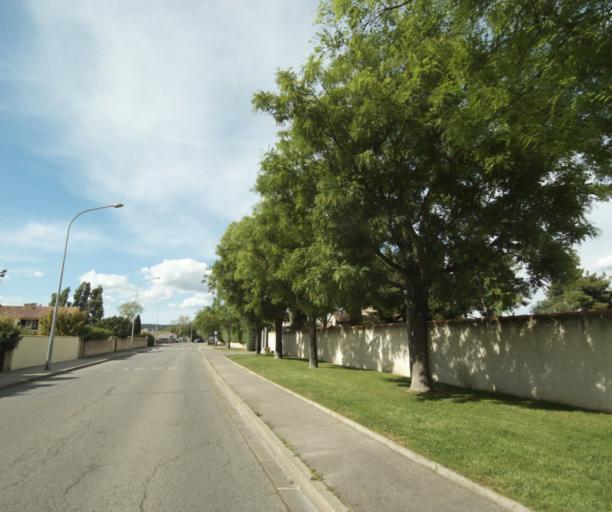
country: FR
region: Provence-Alpes-Cote d'Azur
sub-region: Departement des Bouches-du-Rhone
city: Rognac
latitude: 43.4909
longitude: 5.2219
